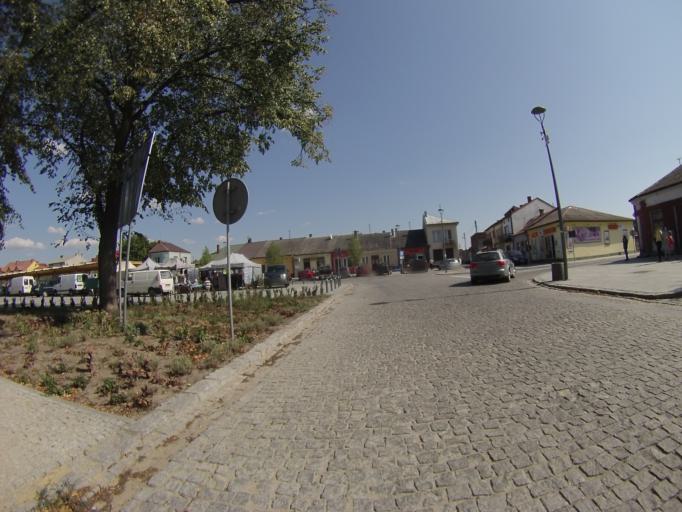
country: PL
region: Swietokrzyskie
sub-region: Powiat kielecki
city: Rakow
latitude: 50.6745
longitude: 21.0429
